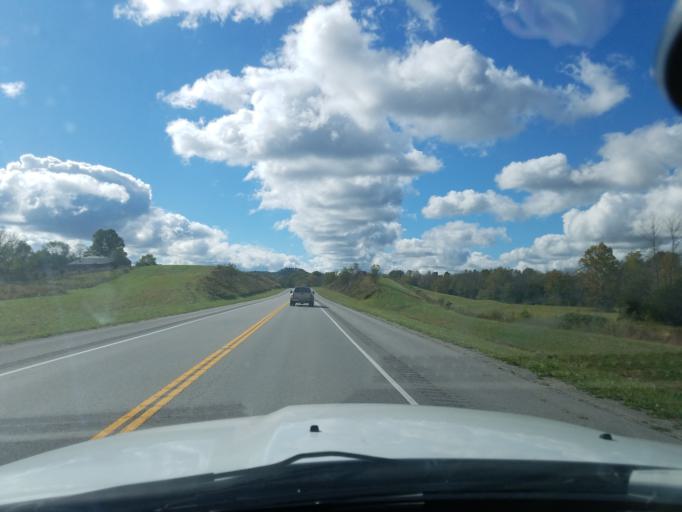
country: US
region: Kentucky
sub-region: Rockcastle County
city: Brodhead
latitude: 37.4639
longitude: -84.5199
